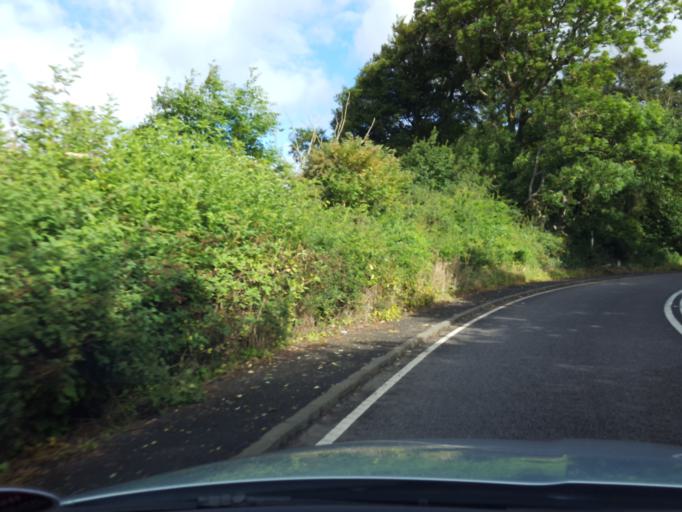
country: GB
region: Scotland
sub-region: West Lothian
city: Linlithgow
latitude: 55.9841
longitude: -3.6141
